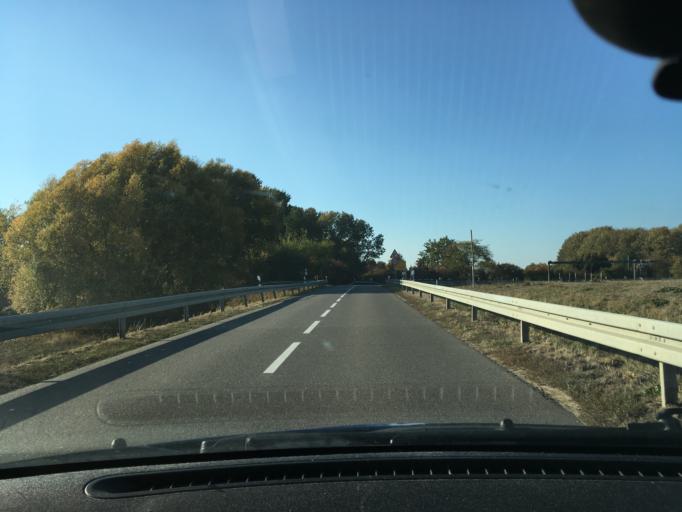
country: DE
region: Mecklenburg-Vorpommern
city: Domitz
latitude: 53.1439
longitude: 11.2658
